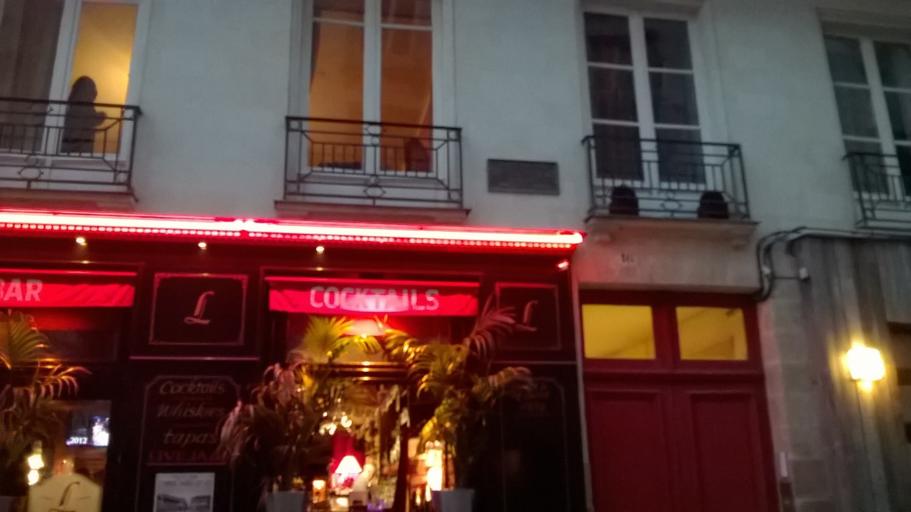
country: FR
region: Pays de la Loire
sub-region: Departement de la Loire-Atlantique
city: Nantes
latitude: 47.2130
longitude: -1.5618
